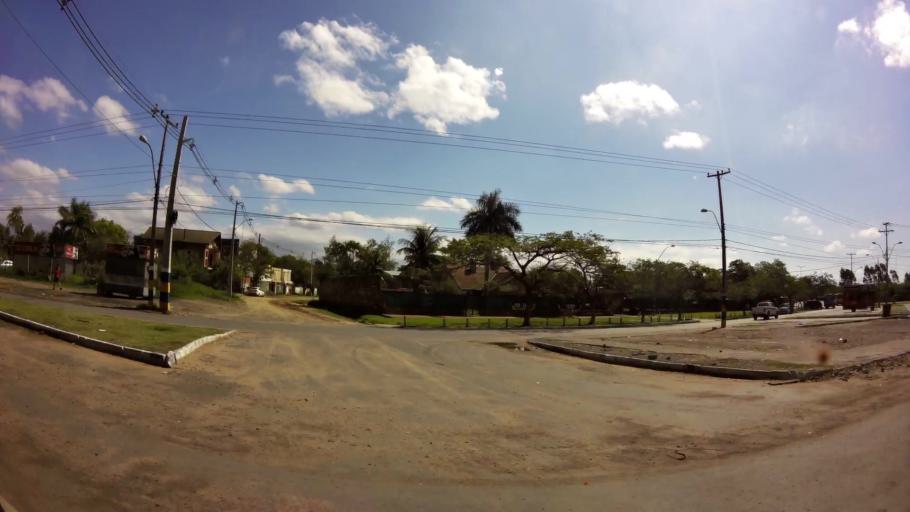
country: PY
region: Central
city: Fernando de la Mora
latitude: -25.2749
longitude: -57.5406
